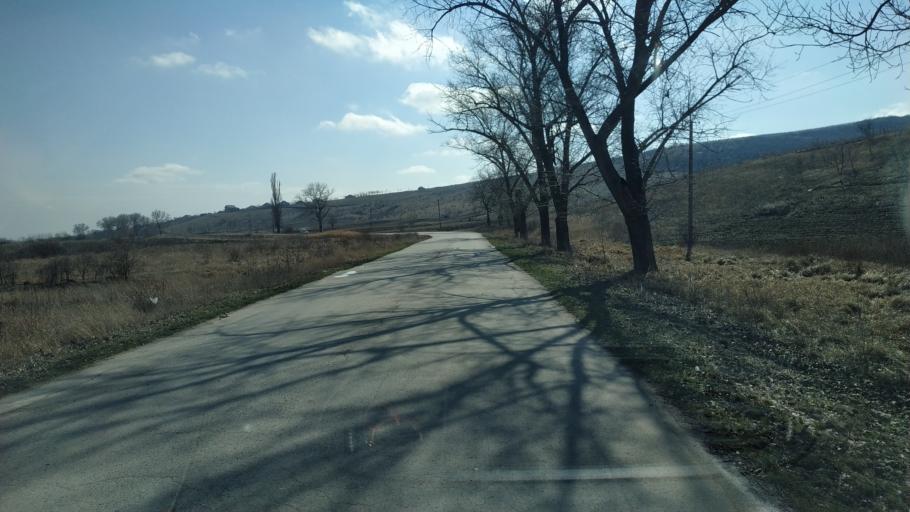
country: MD
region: Hincesti
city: Hincesti
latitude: 46.9432
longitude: 28.6245
